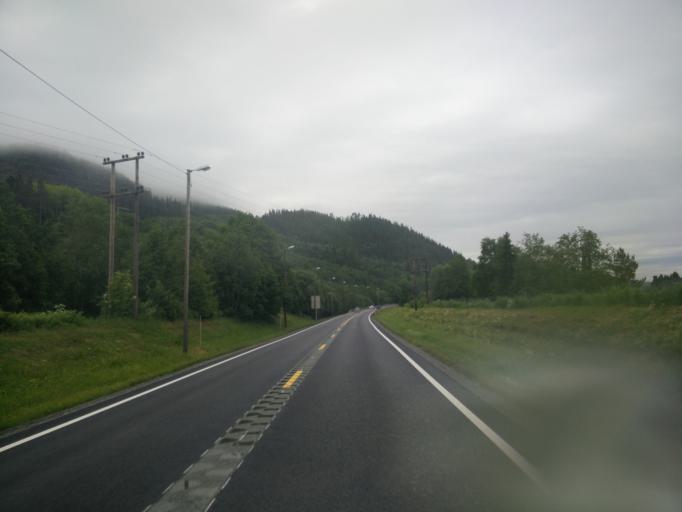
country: NO
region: Sor-Trondelag
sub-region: Orkdal
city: Orkanger
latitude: 63.2863
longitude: 9.8509
